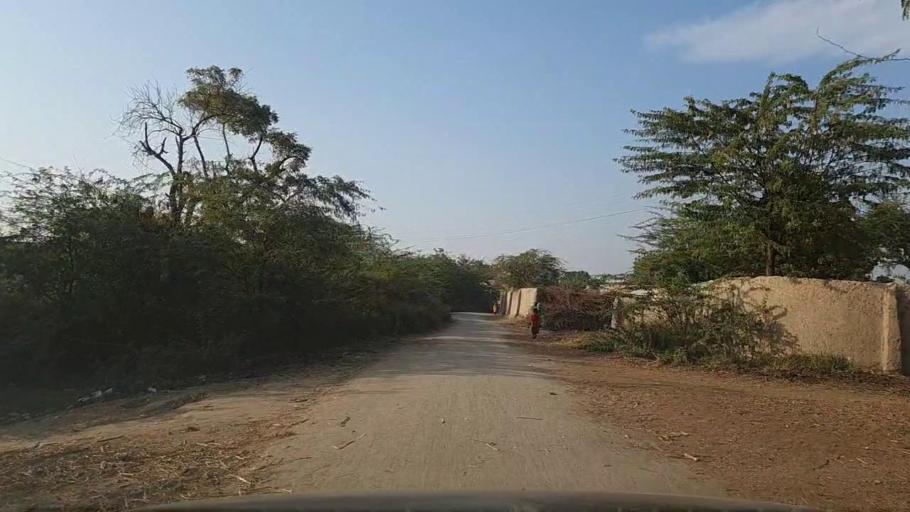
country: PK
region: Sindh
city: Daur
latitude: 26.4140
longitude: 68.4338
